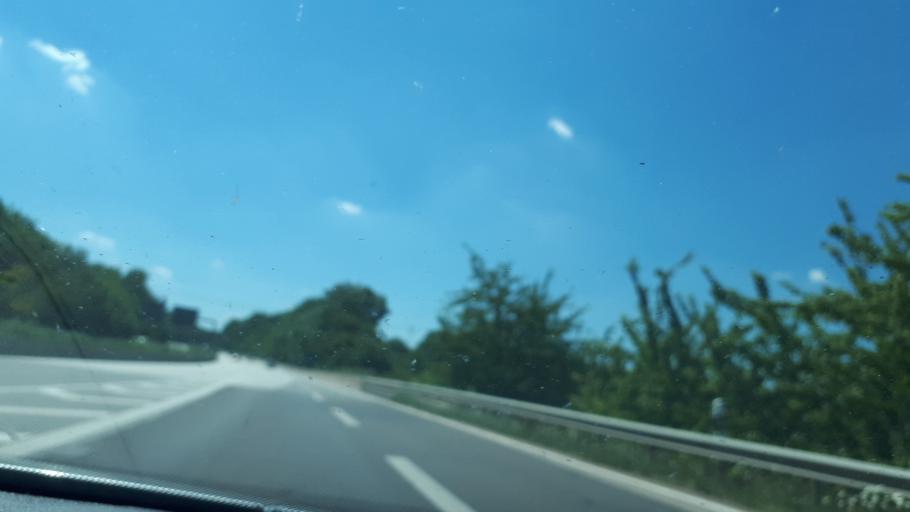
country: DE
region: Rheinland-Pfalz
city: Kaltenengers
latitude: 50.3897
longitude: 7.5406
